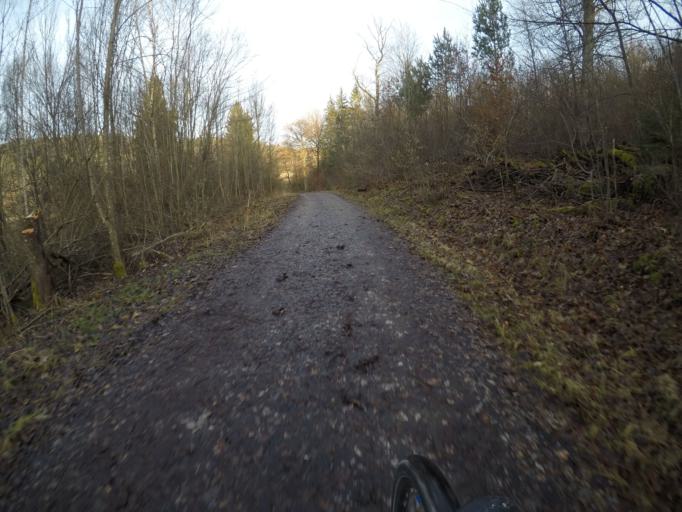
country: DE
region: Baden-Wuerttemberg
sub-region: Regierungsbezirk Stuttgart
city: Schonaich
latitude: 48.6503
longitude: 9.0872
